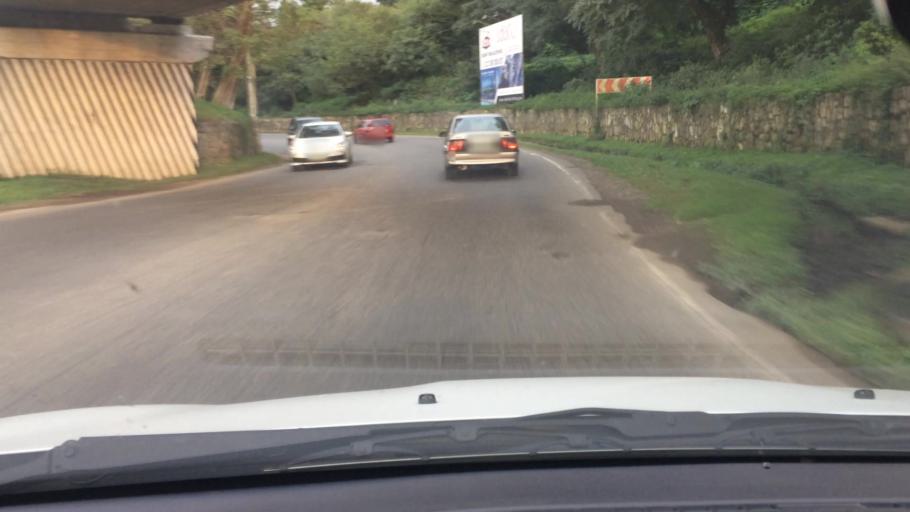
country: GE
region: Ajaria
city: Makhinjauri
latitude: 41.6718
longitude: 41.6902
